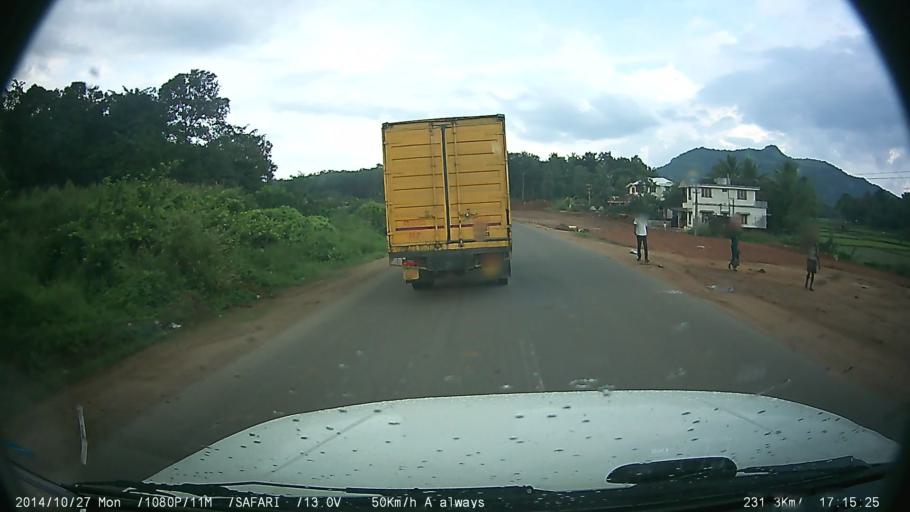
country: IN
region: Kerala
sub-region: Thrissur District
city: Chelakara
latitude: 10.6218
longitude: 76.5104
